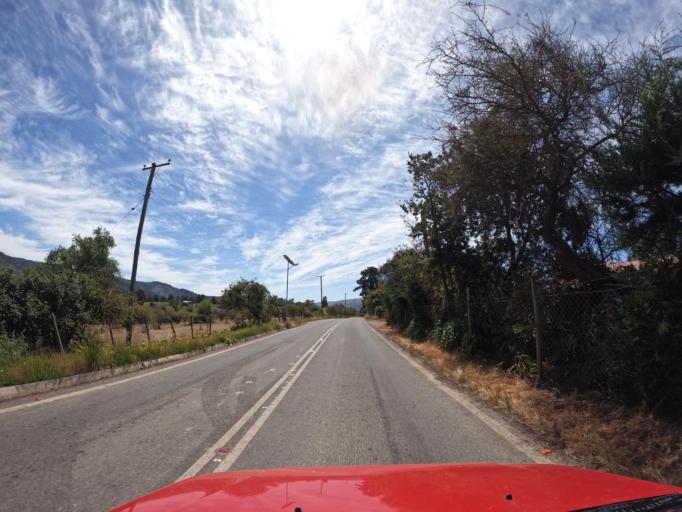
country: CL
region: Maule
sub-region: Provincia de Talca
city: Talca
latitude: -35.0109
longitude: -71.7849
